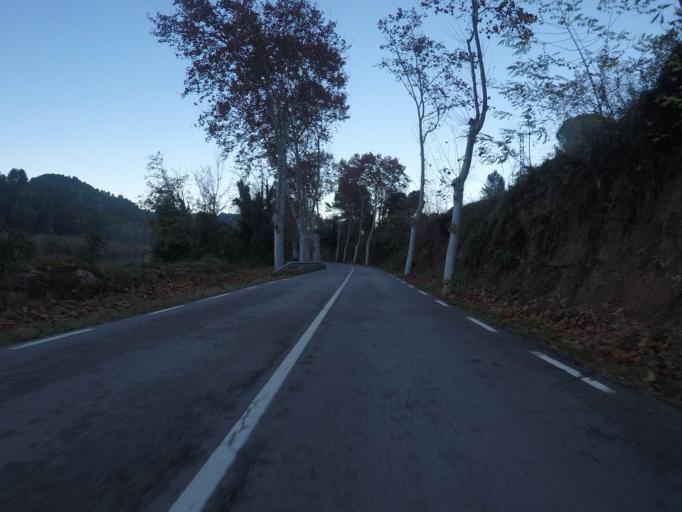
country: ES
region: Catalonia
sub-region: Provincia de Barcelona
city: Monistrol de Montserrat
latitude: 41.6154
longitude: 1.8517
